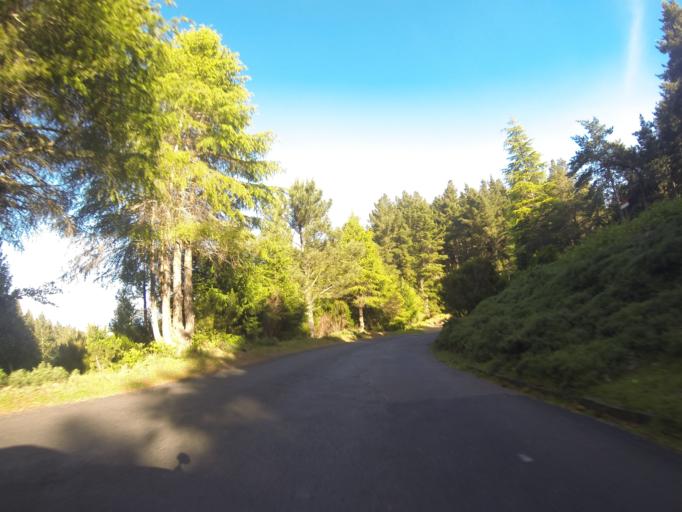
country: PT
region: Madeira
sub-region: Funchal
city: Nossa Senhora do Monte
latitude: 32.7007
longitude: -16.8832
